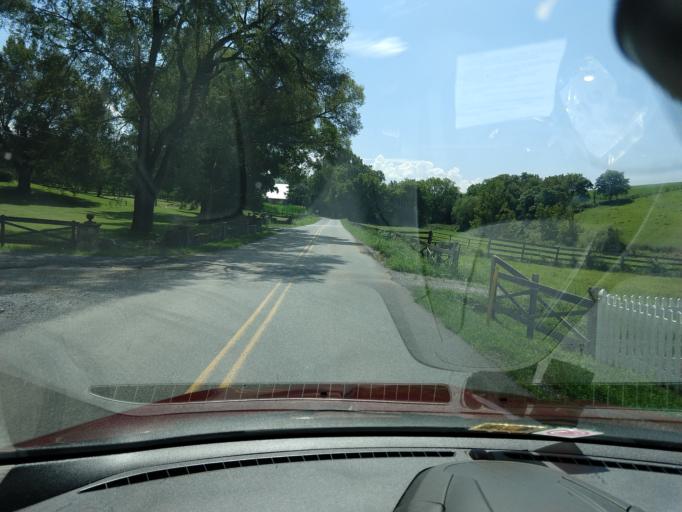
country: US
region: Virginia
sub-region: City of Harrisonburg
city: Harrisonburg
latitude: 38.5274
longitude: -78.8641
